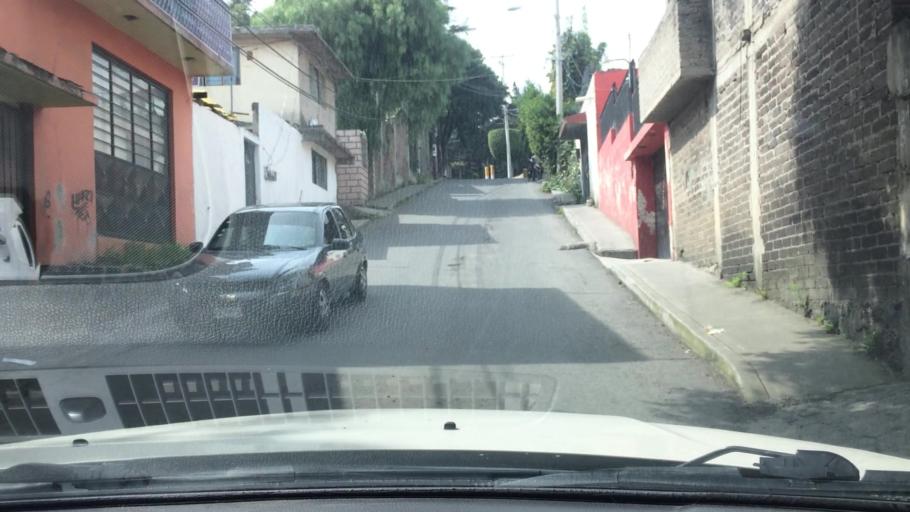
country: MX
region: Mexico City
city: Xochimilco
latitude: 19.2387
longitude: -99.1495
